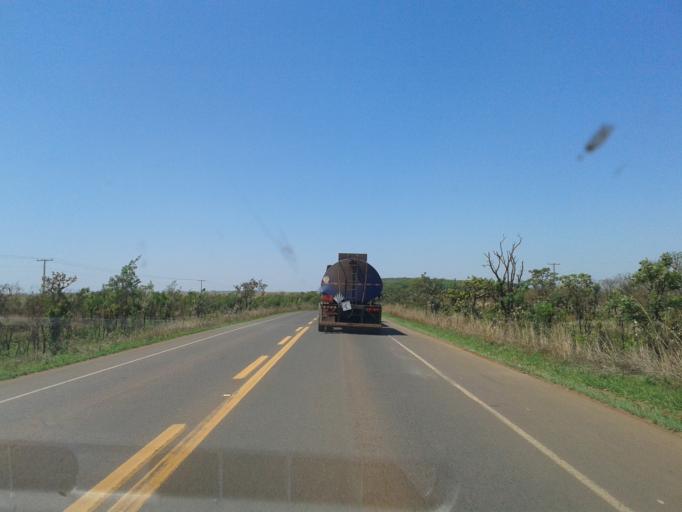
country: BR
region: Minas Gerais
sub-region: Araxa
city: Araxa
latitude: -19.3232
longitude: -47.3832
